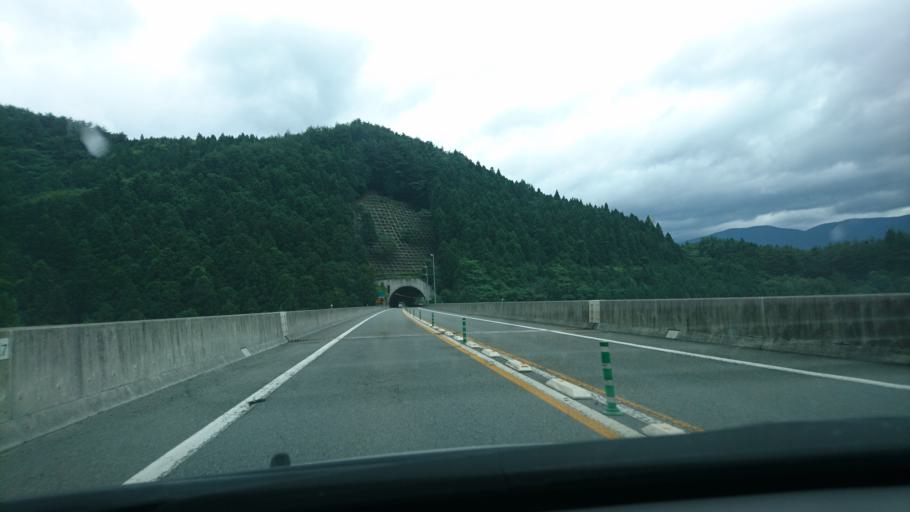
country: JP
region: Iwate
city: Ofunato
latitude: 39.0748
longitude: 141.7030
